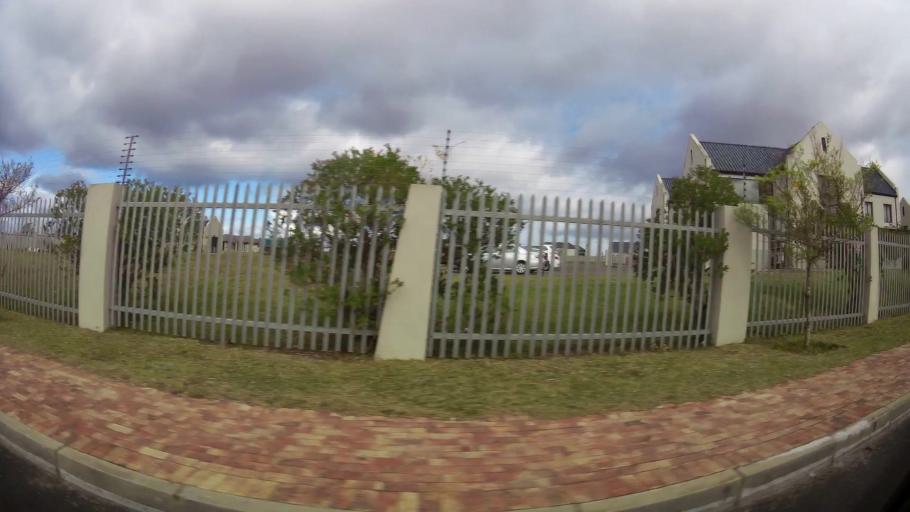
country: ZA
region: Western Cape
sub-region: Eden District Municipality
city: George
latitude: -33.9815
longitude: 22.4952
